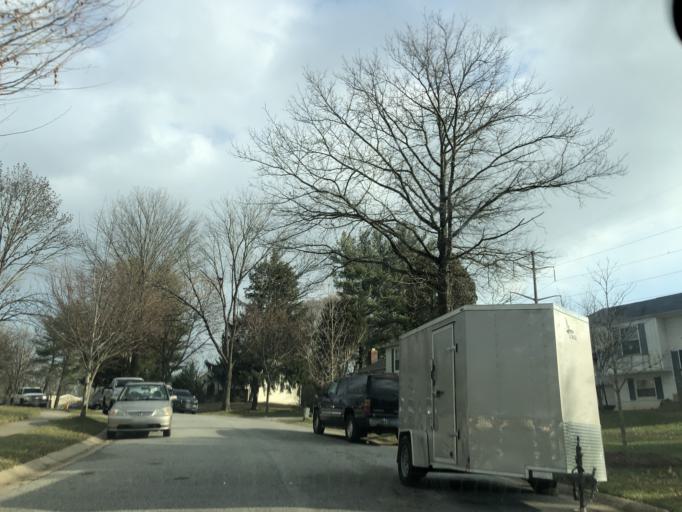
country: US
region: Maryland
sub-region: Howard County
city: Columbia
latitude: 39.1968
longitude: -76.8385
